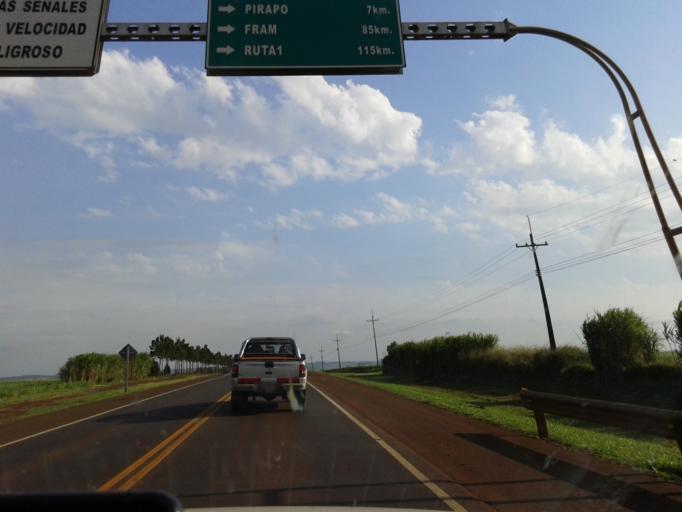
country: PY
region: Itapua
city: Pirapo
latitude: -26.9013
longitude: -55.4757
